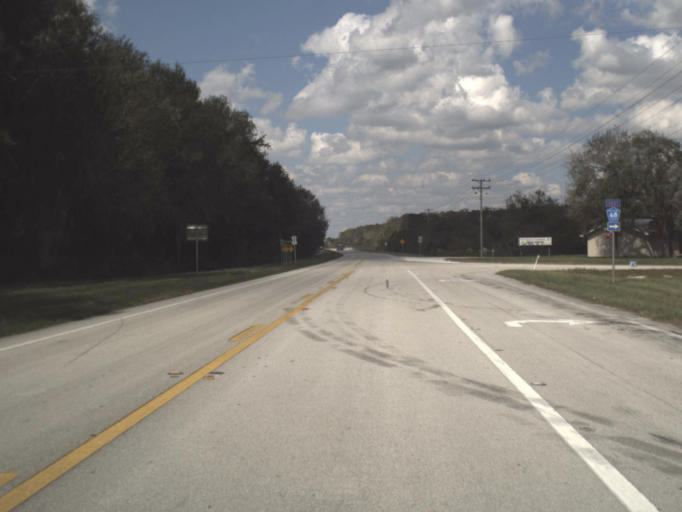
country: US
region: Florida
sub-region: Okeechobee County
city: Okeechobee
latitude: 27.3755
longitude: -80.9833
